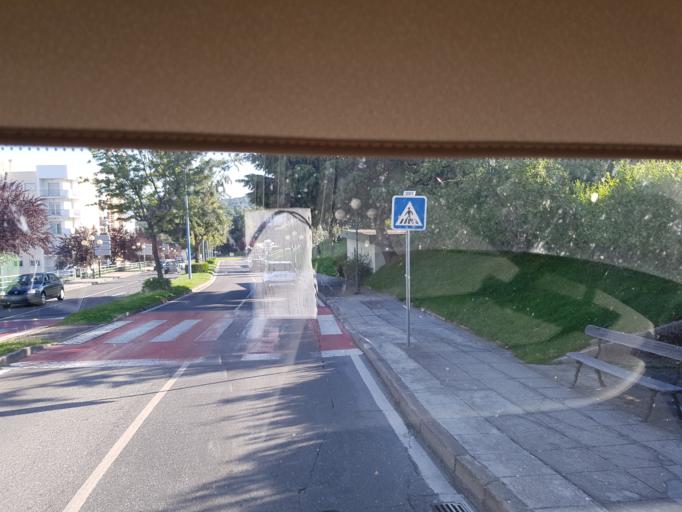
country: PT
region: Castelo Branco
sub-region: Covilha
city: Covilha
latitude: 40.2731
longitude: -7.5029
